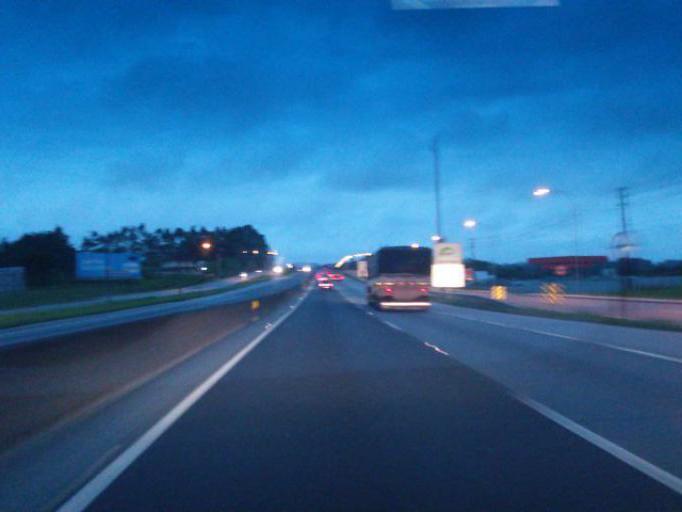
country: BR
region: Santa Catarina
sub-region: Penha
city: Penha
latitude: -26.7669
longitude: -48.6863
